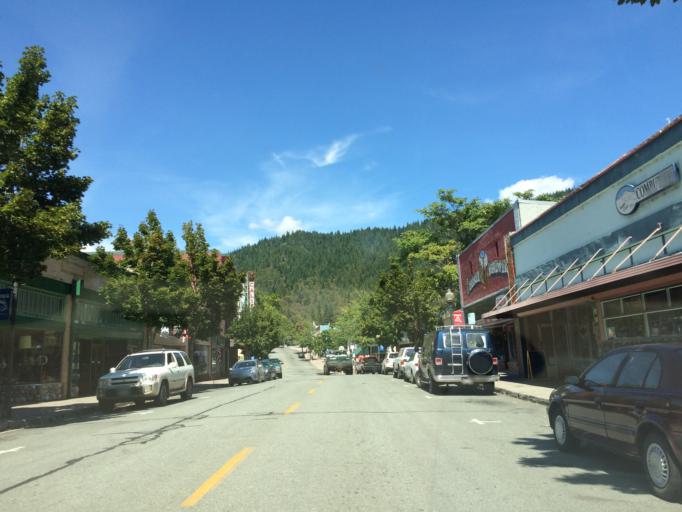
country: US
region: California
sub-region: Siskiyou County
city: Dunsmuir
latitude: 41.2102
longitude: -122.2724
